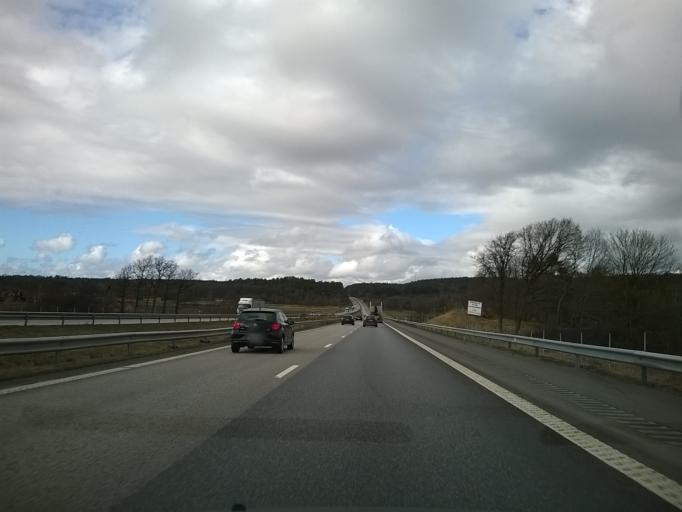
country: SE
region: Halland
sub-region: Kungsbacka Kommun
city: Frillesas
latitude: 57.2961
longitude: 12.2158
